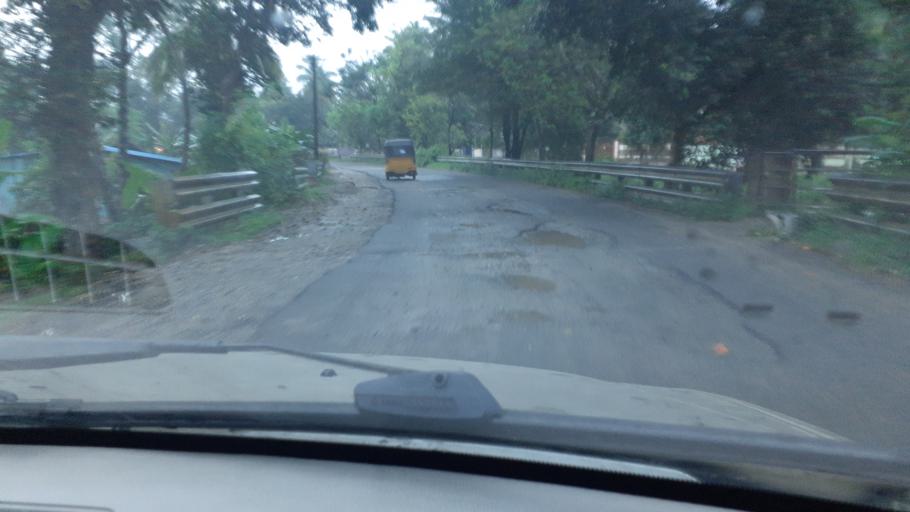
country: IN
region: Tamil Nadu
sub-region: Kanniyakumari
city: Padmanabhapuram
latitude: 8.3622
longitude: 77.3150
